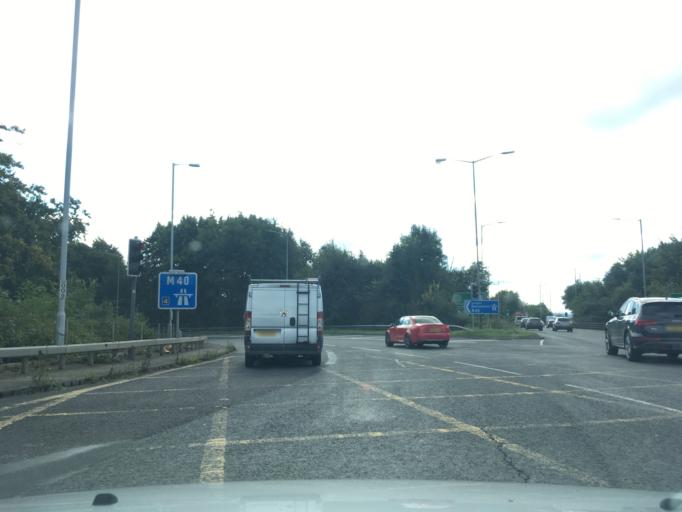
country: GB
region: England
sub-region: Buckinghamshire
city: High Wycombe
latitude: 51.6133
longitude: -0.7680
